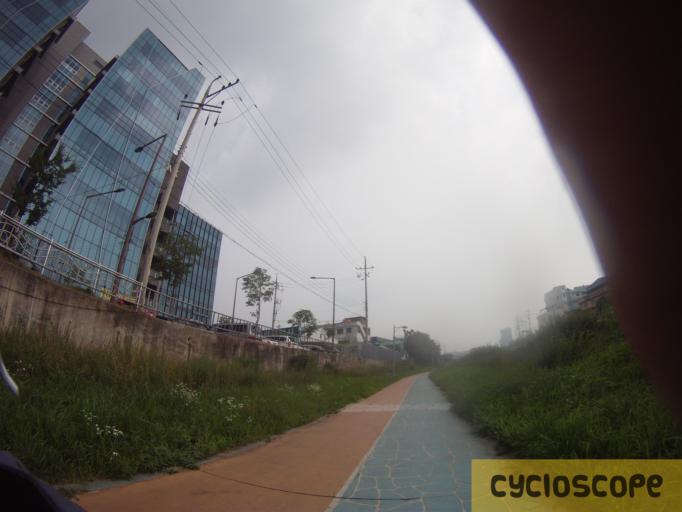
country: KR
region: Gyeonggi-do
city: Anyang-si
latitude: 37.3621
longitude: 126.9565
